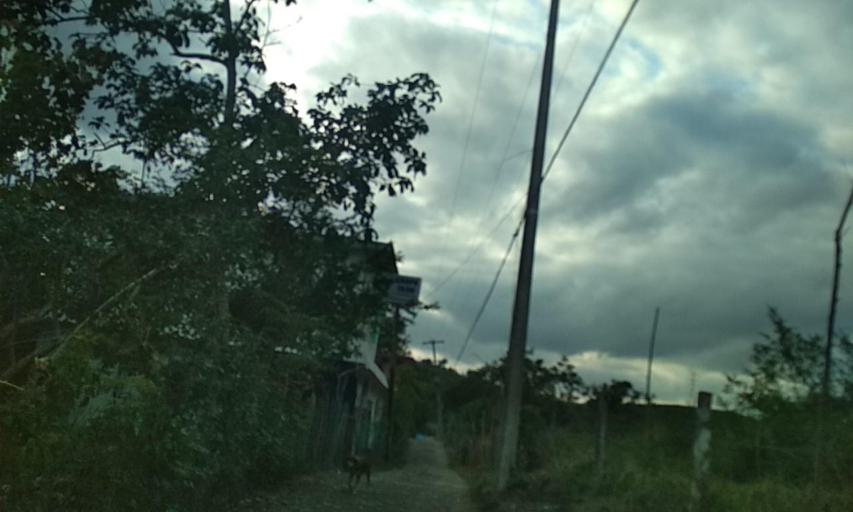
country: MX
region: Veracruz
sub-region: Papantla
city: El Chote
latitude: 20.4314
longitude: -97.3822
